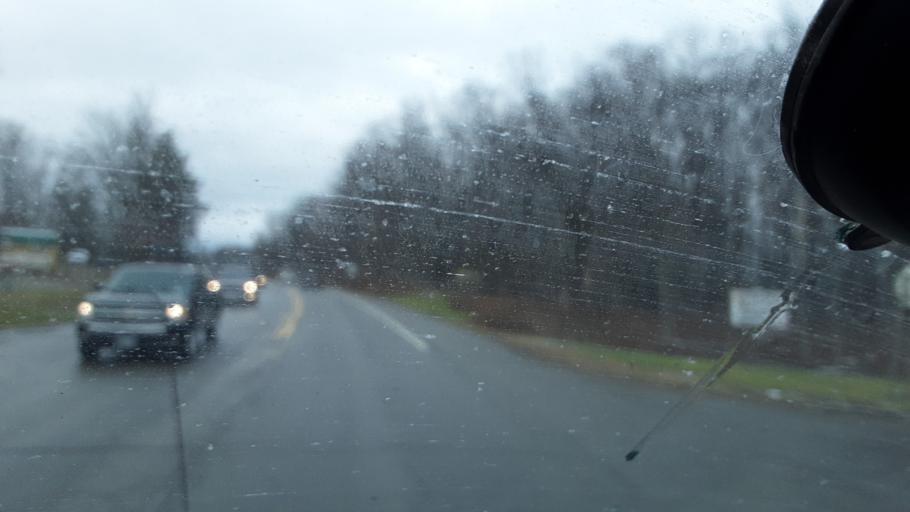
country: US
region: New York
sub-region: Cattaraugus County
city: Yorkshire
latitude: 42.5128
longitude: -78.4785
